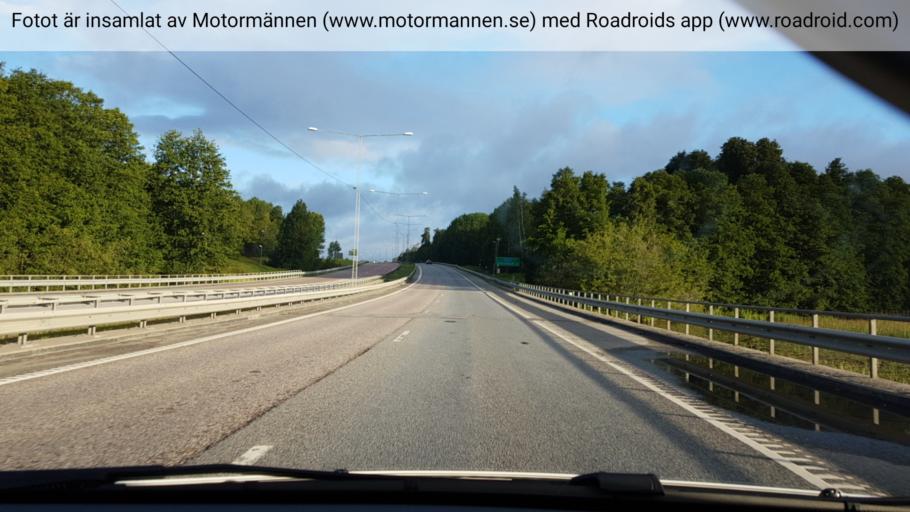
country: SE
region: Stockholm
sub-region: Nacka Kommun
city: Alta
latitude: 59.2569
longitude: 18.1682
